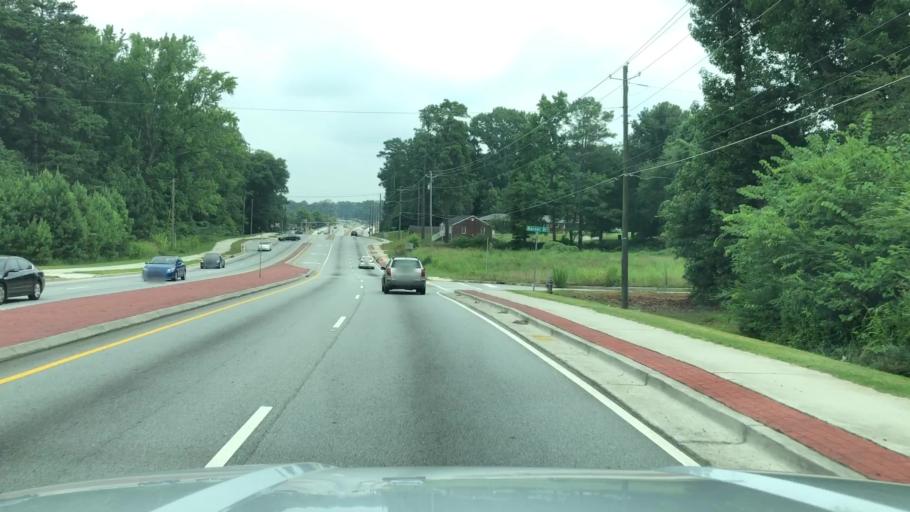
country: US
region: Georgia
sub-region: Cobb County
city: Mableton
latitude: 33.8275
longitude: -84.5756
